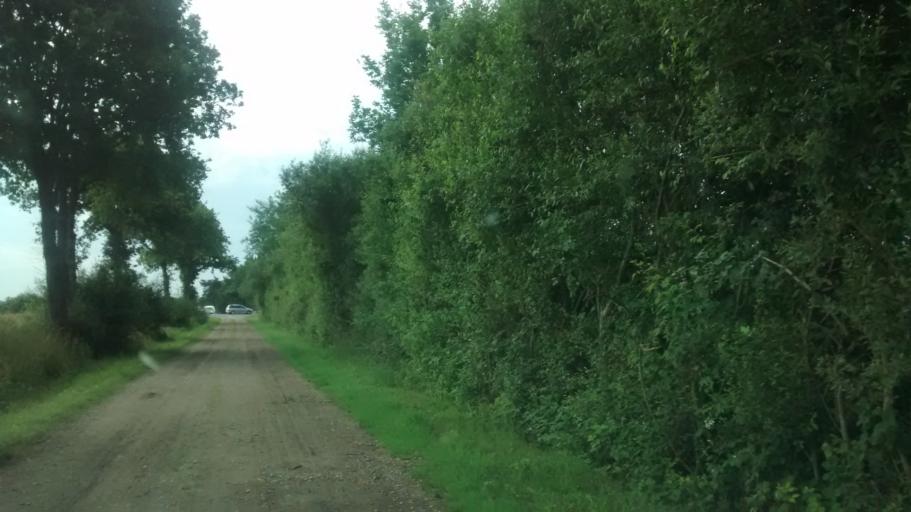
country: FR
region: Brittany
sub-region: Departement d'Ille-et-Vilaine
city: Plechatel
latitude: 47.8336
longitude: -1.7465
